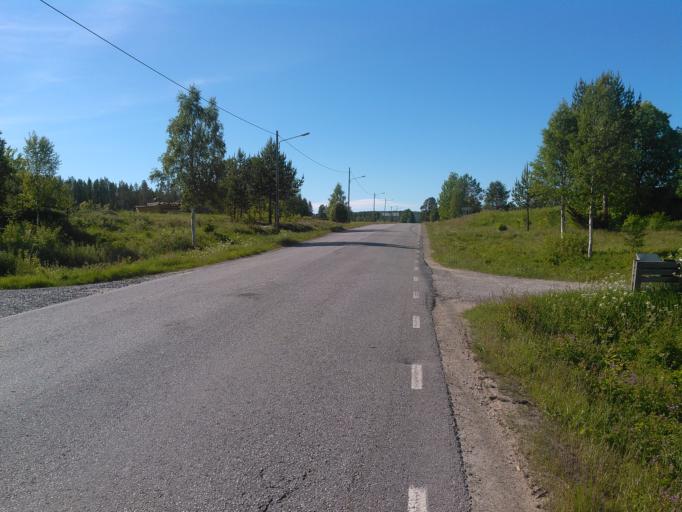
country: SE
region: Vaesterbotten
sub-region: Umea Kommun
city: Roback
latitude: 63.8261
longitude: 20.1212
